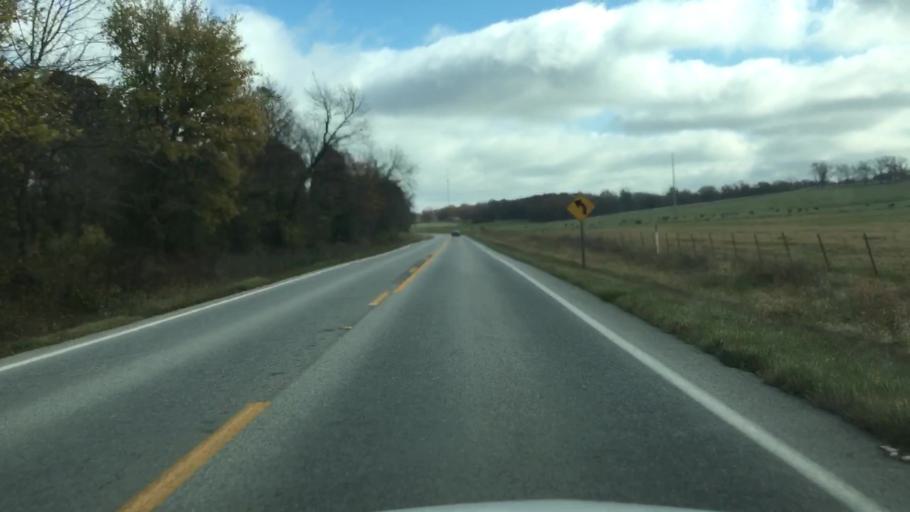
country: US
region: Arkansas
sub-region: Benton County
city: Gentry
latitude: 36.2584
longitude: -94.4076
